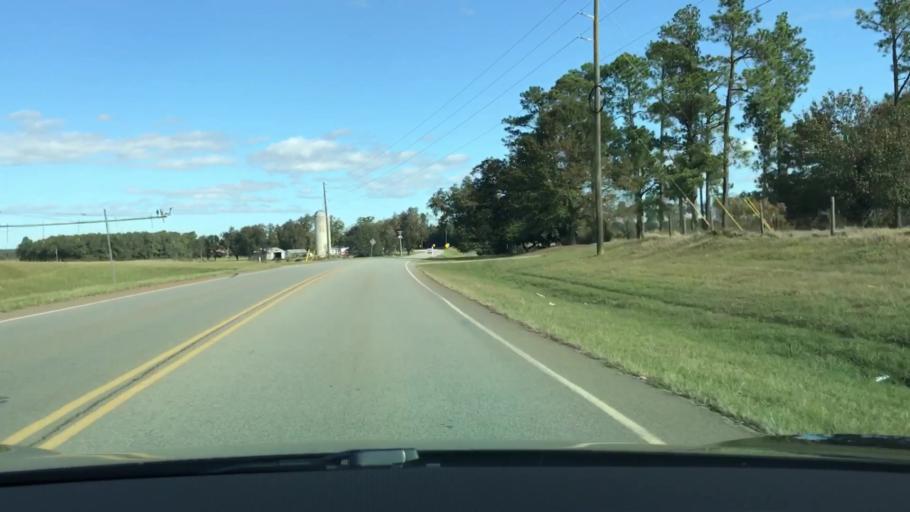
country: US
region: Georgia
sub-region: Jefferson County
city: Wrens
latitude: 33.1515
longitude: -82.4572
